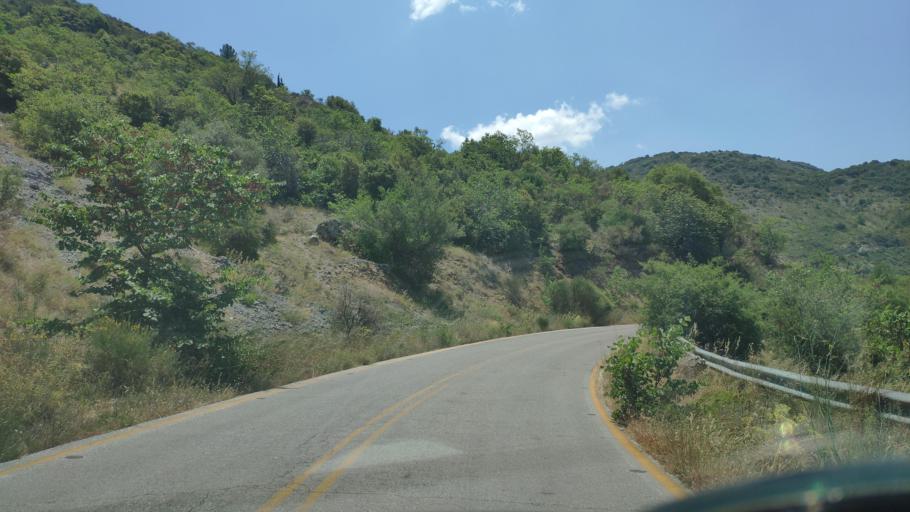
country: GR
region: Ionian Islands
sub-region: Lefkada
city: Nidri
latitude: 38.7496
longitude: 20.6208
